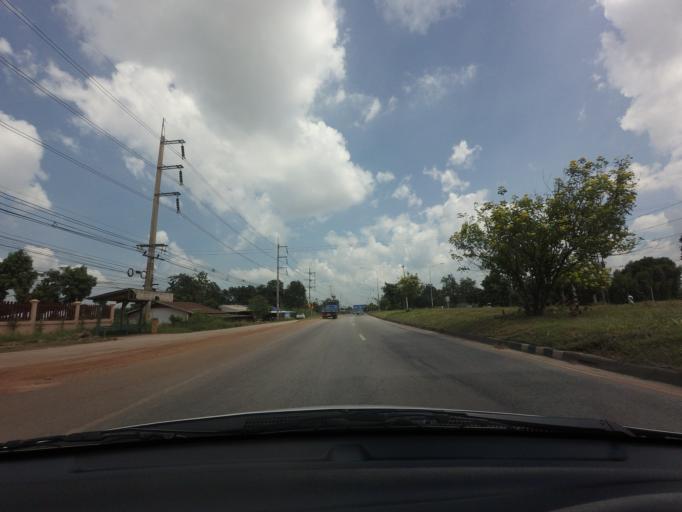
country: TH
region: Chachoengsao
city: Sanam Chai Khet
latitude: 13.7863
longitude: 101.5294
